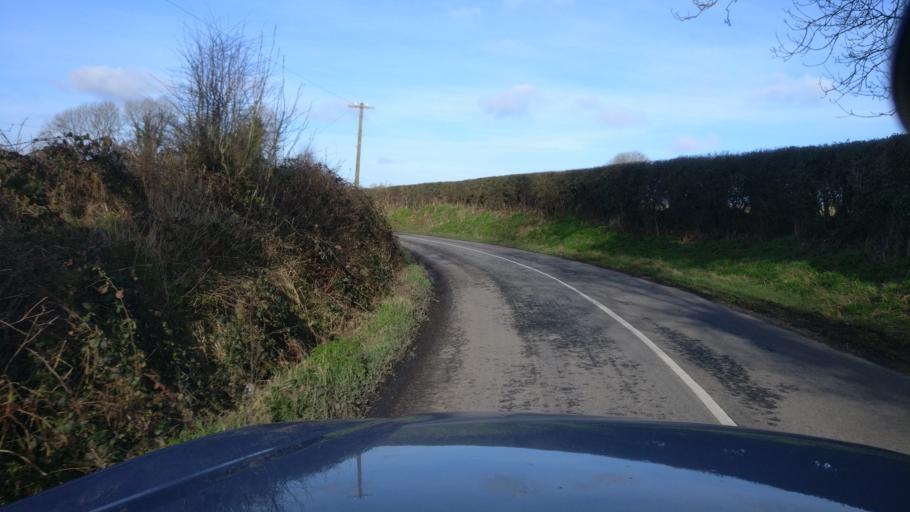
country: IE
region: Leinster
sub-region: Kilkenny
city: Castlecomer
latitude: 52.8808
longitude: -7.1633
